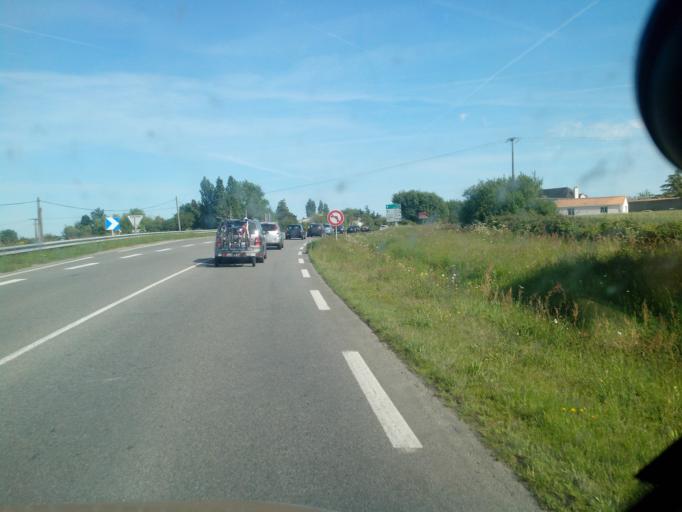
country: FR
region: Pays de la Loire
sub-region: Departement de la Loire-Atlantique
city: Port-Saint-Pere
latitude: 47.1333
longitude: -1.7595
